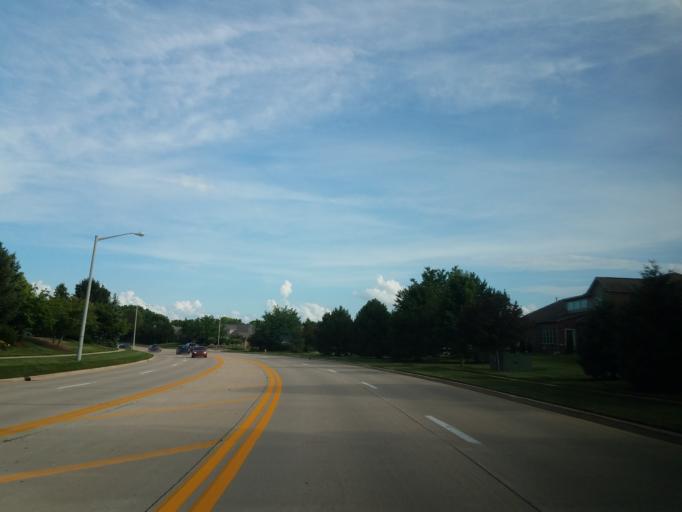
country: US
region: Illinois
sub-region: McLean County
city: Normal
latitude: 40.5068
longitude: -88.9420
